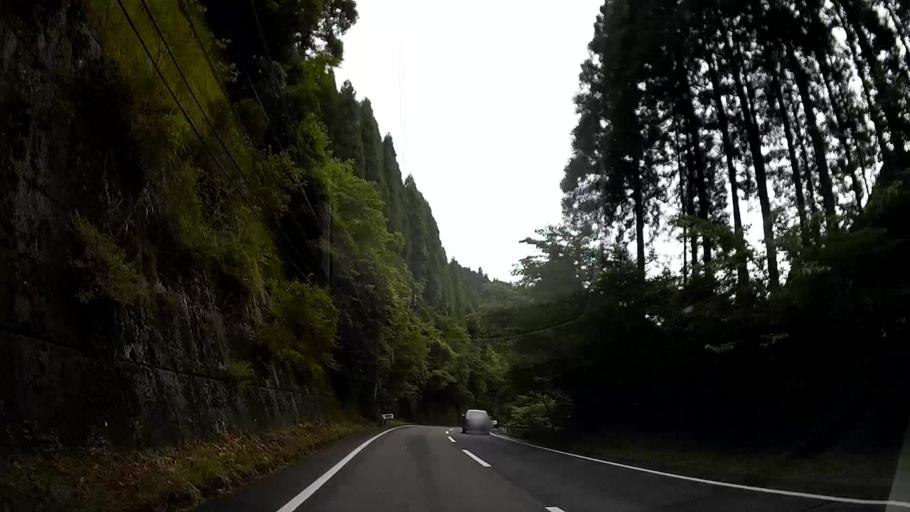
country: JP
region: Kumamoto
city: Kikuchi
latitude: 33.0774
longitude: 130.9316
